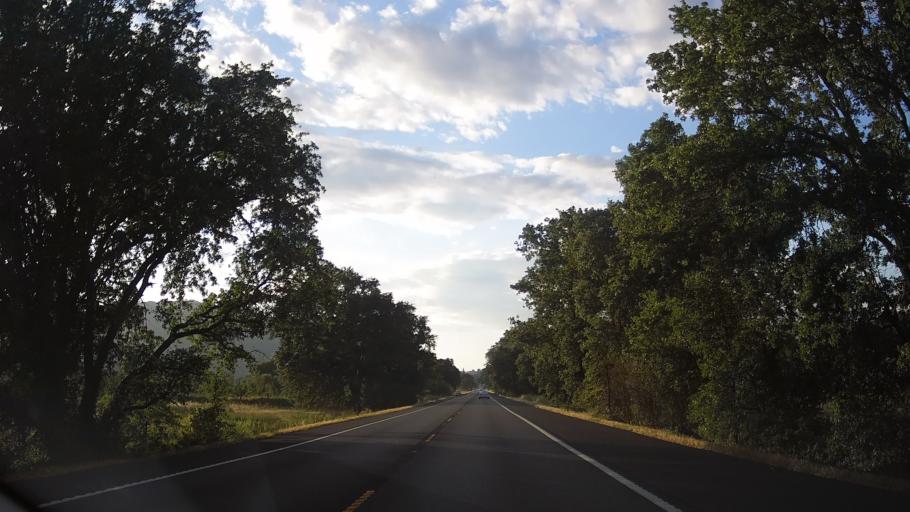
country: US
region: California
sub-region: Mendocino County
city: Talmage
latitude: 39.0357
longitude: -123.1444
